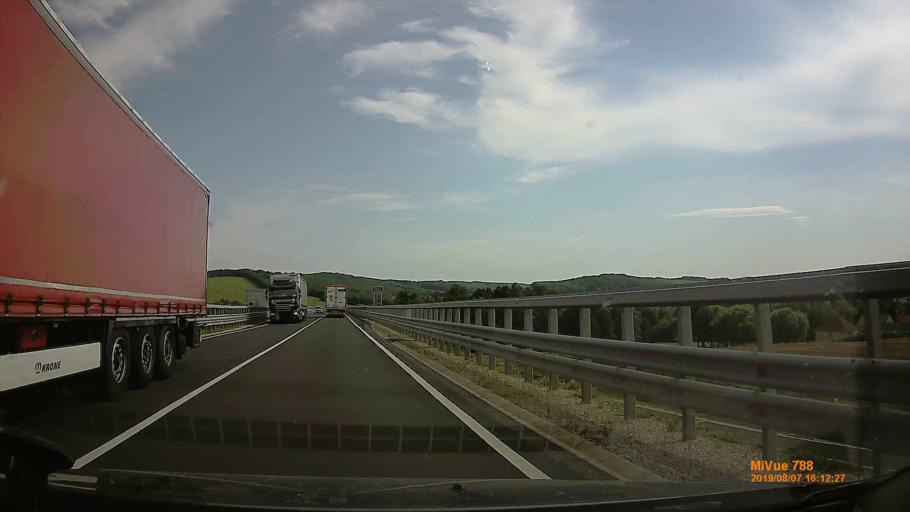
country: HU
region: Zala
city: Zalalovo
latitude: 46.8553
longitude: 16.6279
